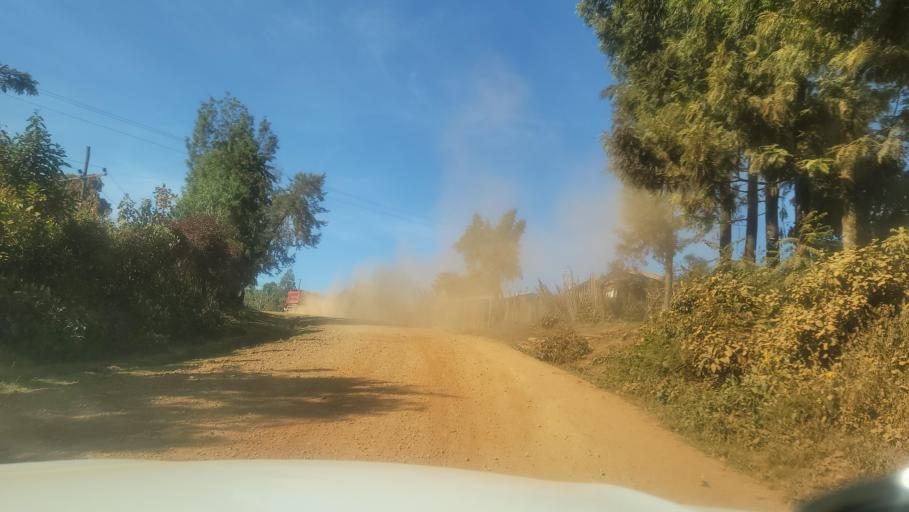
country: ET
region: Oromiya
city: Agaro
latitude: 7.8146
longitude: 36.5077
